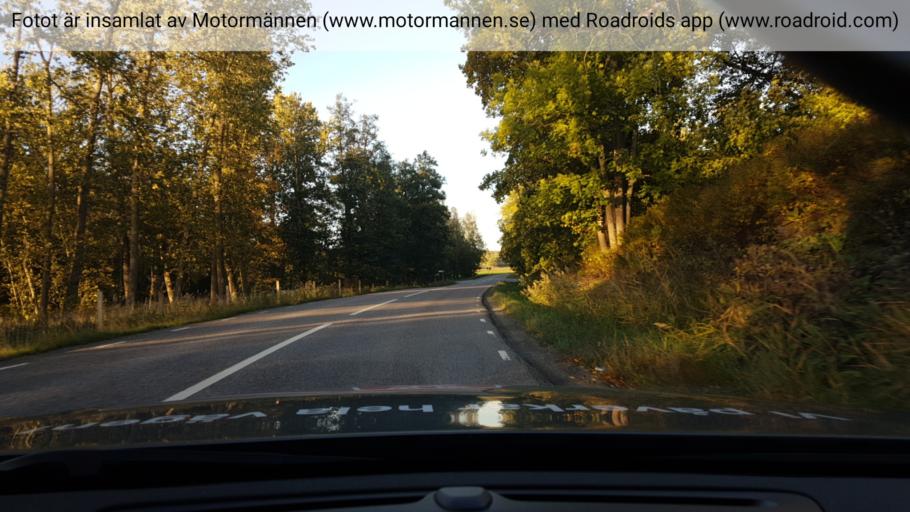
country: SE
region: Stockholm
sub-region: Haninge Kommun
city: Jordbro
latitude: 59.1752
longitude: 18.0739
